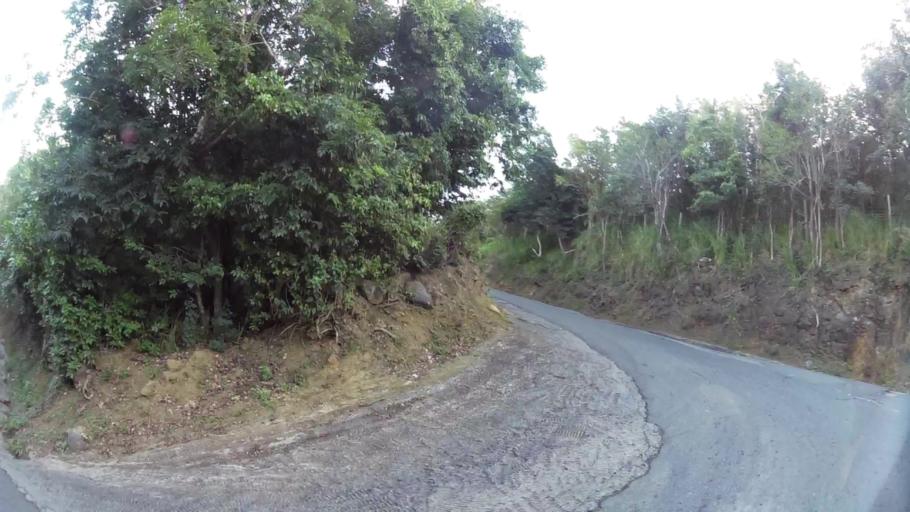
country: VG
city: Road Town
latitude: 18.4371
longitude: -64.6363
